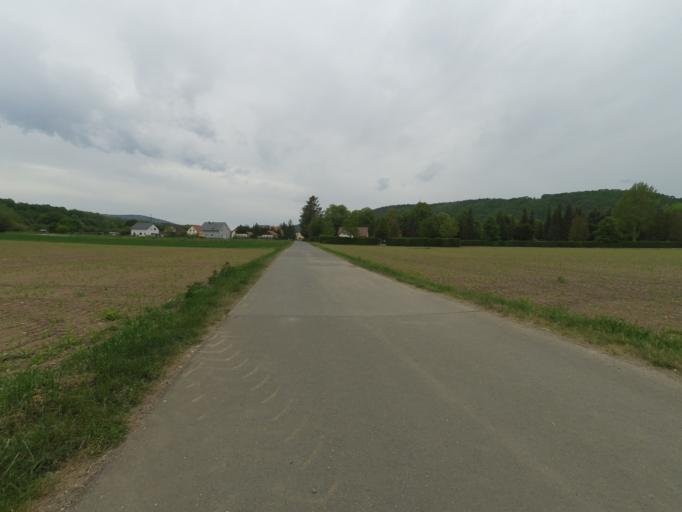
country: DE
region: Thuringia
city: Rudolstadt
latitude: 50.6826
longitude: 11.3192
